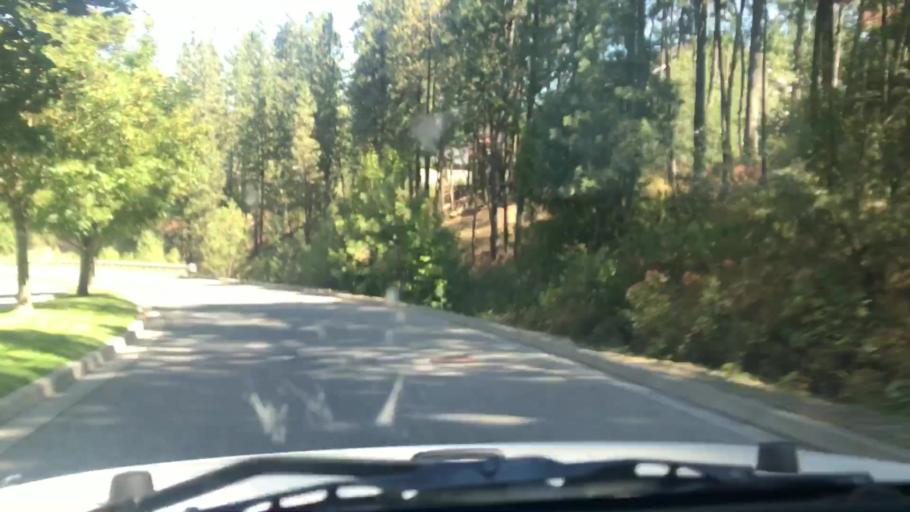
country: US
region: Washington
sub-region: Spokane County
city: Spokane
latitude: 47.5954
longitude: -117.4164
